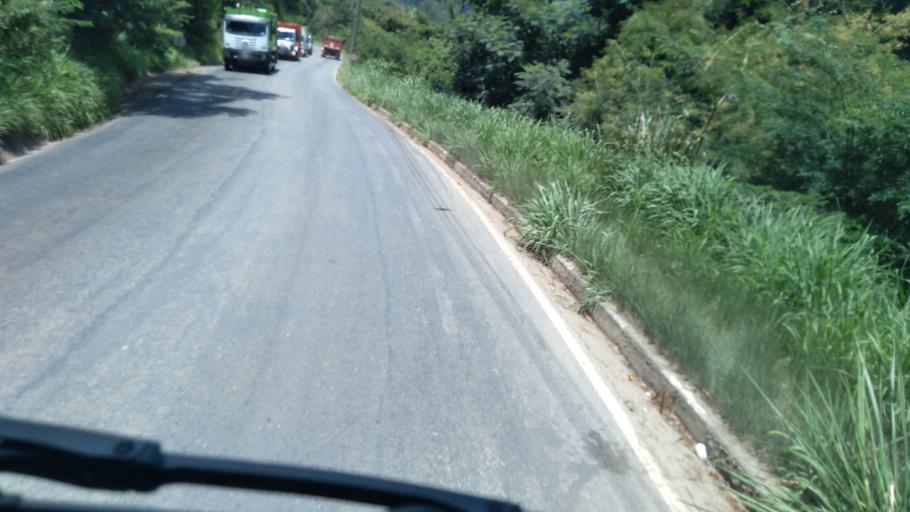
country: BR
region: Minas Gerais
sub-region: Santa Luzia
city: Santa Luzia
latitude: -19.8579
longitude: -43.8495
